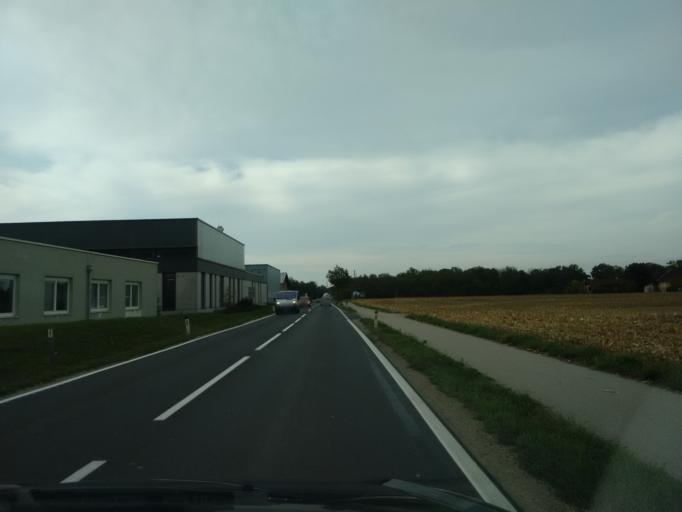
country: AT
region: Upper Austria
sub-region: Wels-Land
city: Marchtrenk
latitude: 48.1682
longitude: 14.1277
